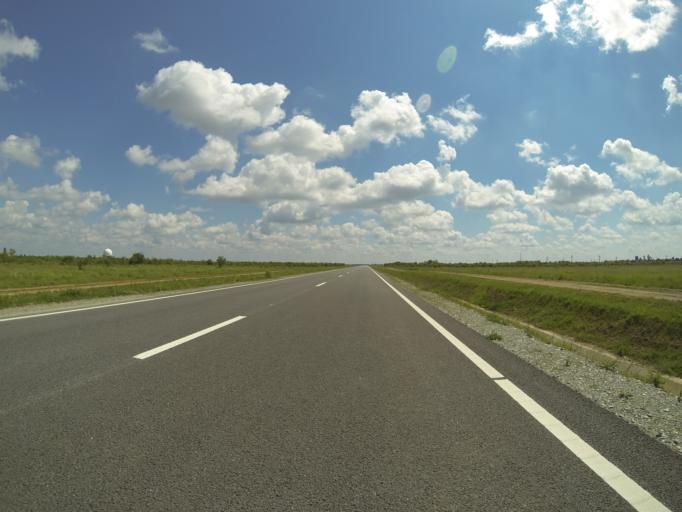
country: RO
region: Dolj
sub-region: Comuna Carcea
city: Carcea
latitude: 44.2807
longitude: 23.9074
